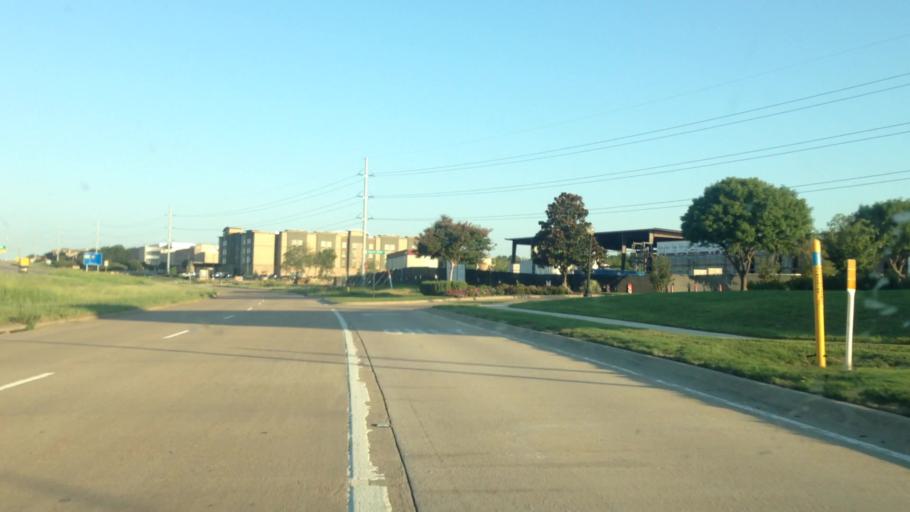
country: US
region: Texas
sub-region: Denton County
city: Trophy Club
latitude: 32.9861
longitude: -97.1705
